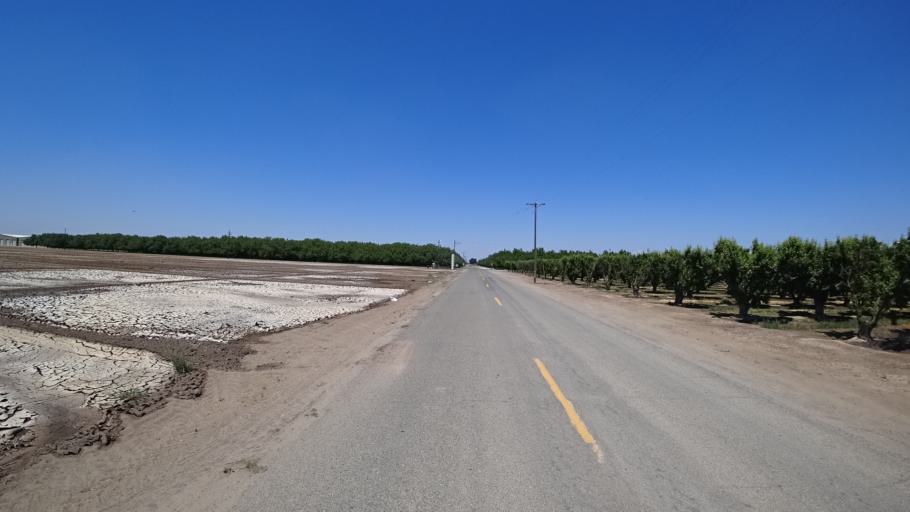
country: US
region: California
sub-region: Kings County
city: Lucerne
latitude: 36.4000
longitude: -119.6190
